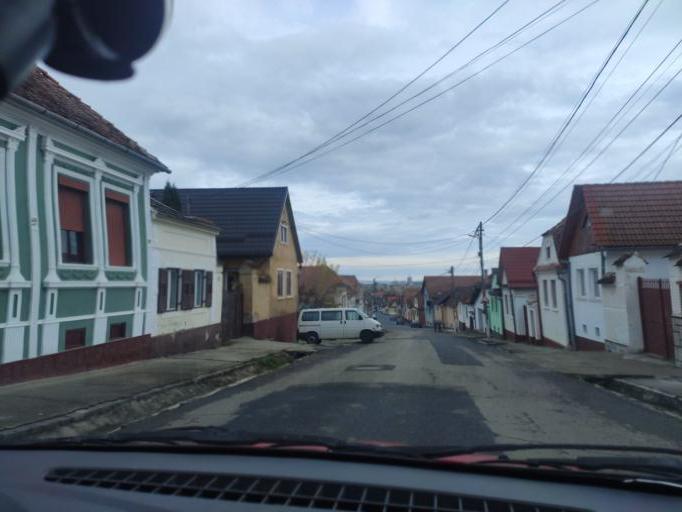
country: RO
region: Brasov
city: Codlea
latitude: 45.6980
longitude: 25.4378
